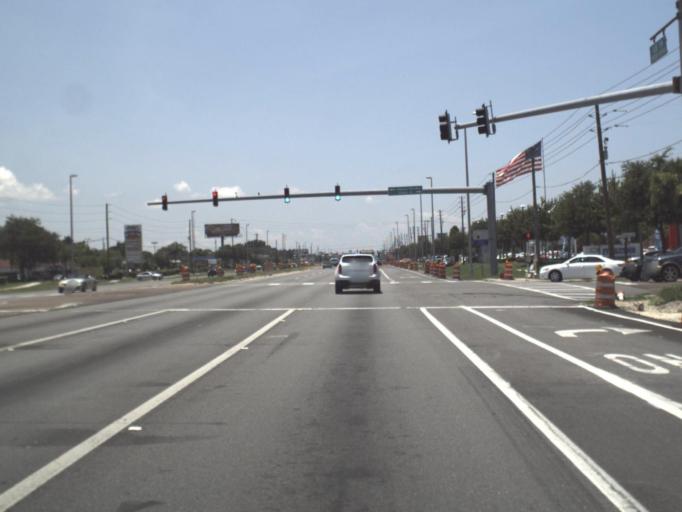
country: US
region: Florida
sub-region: Pasco County
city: Jasmine Estates
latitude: 28.3067
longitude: -82.7016
